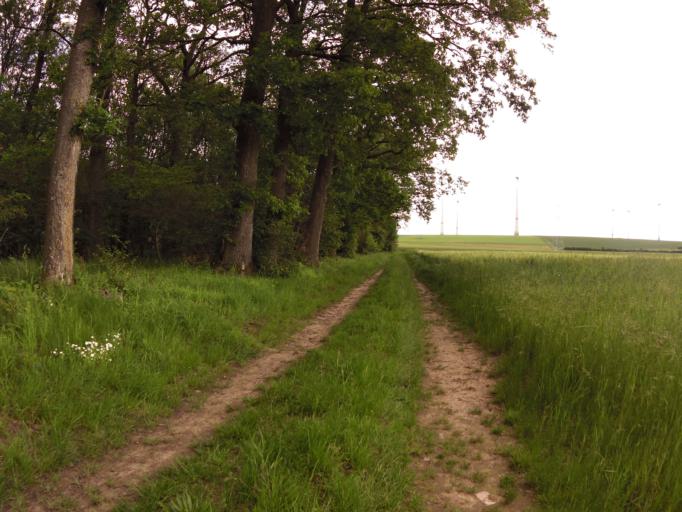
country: DE
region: Bavaria
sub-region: Regierungsbezirk Unterfranken
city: Theilheim
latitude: 49.7301
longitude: 10.0508
